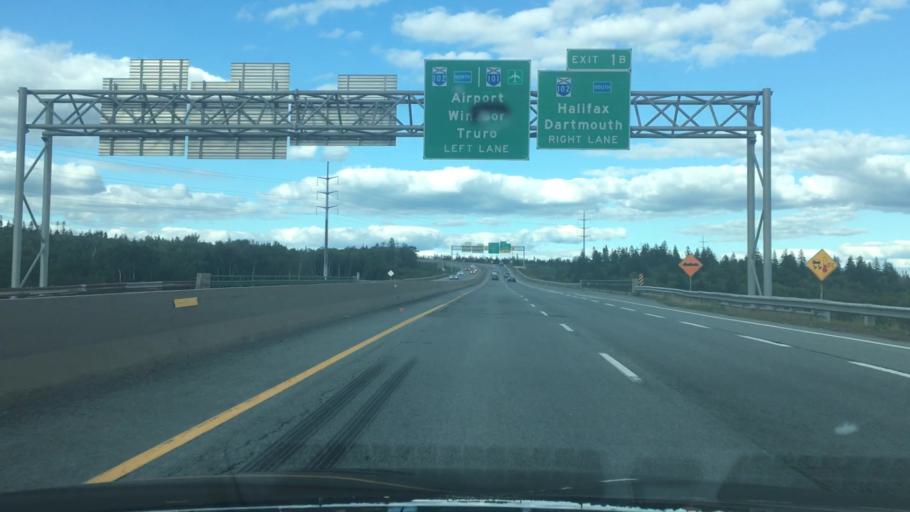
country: CA
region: Nova Scotia
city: Halifax
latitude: 44.6388
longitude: -63.6593
